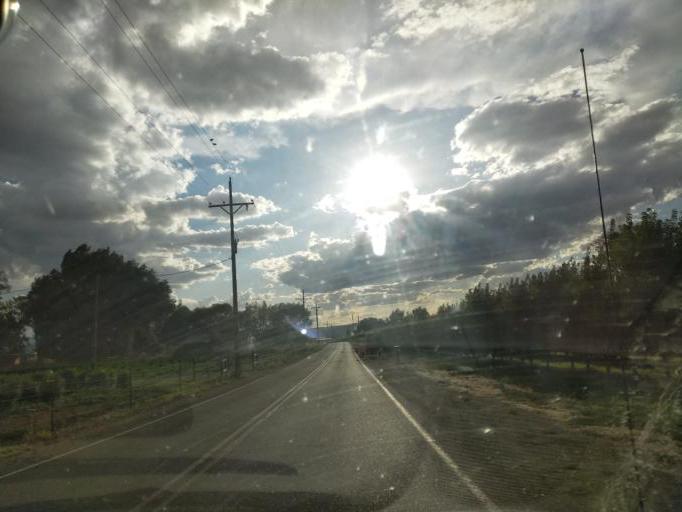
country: US
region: Colorado
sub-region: Mesa County
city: Clifton
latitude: 39.0558
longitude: -108.4136
